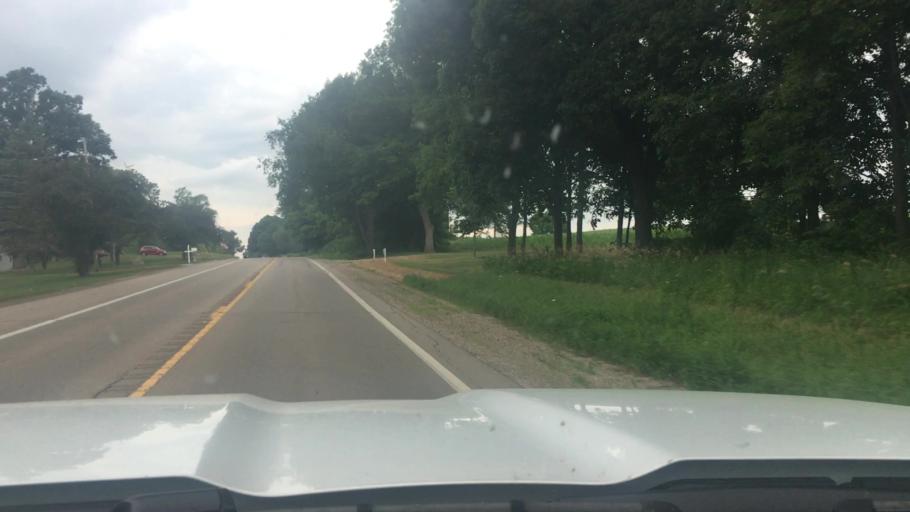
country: US
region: Michigan
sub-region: Ionia County
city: Ionia
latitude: 43.0017
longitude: -84.9575
